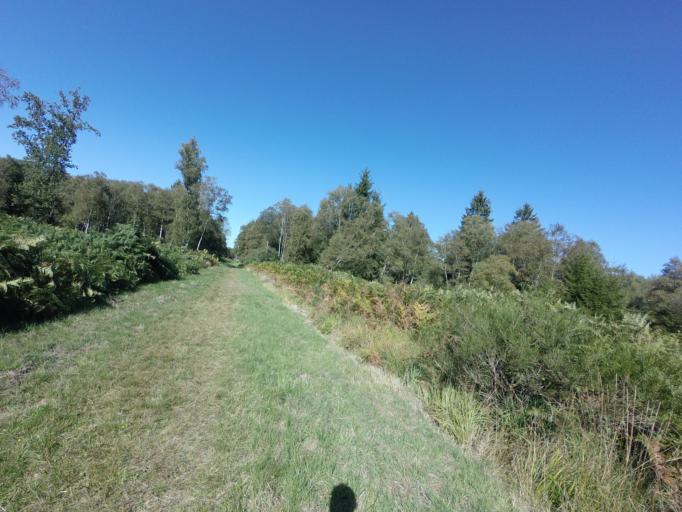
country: DE
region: North Rhine-Westphalia
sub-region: Regierungsbezirk Koln
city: Roetgen
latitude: 50.6019
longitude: 6.1710
